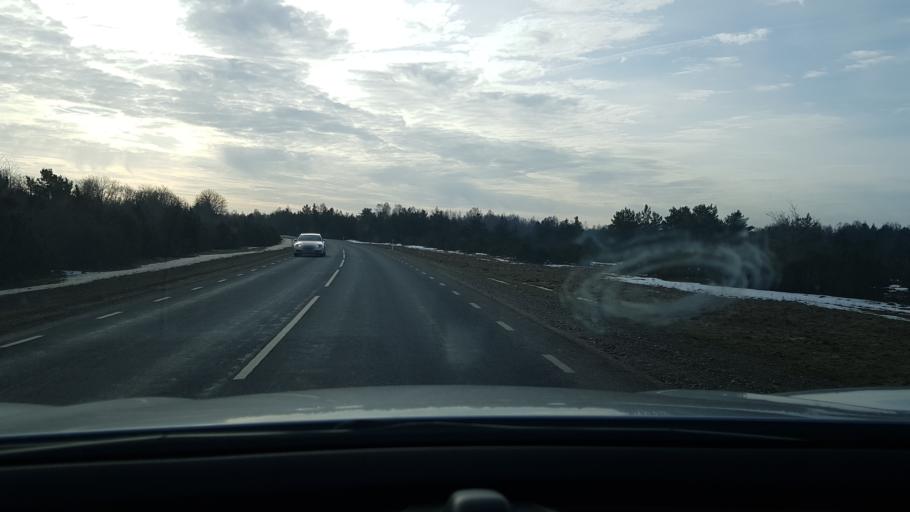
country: EE
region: Saare
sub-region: Kuressaare linn
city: Kuressaare
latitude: 58.2889
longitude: 22.5396
